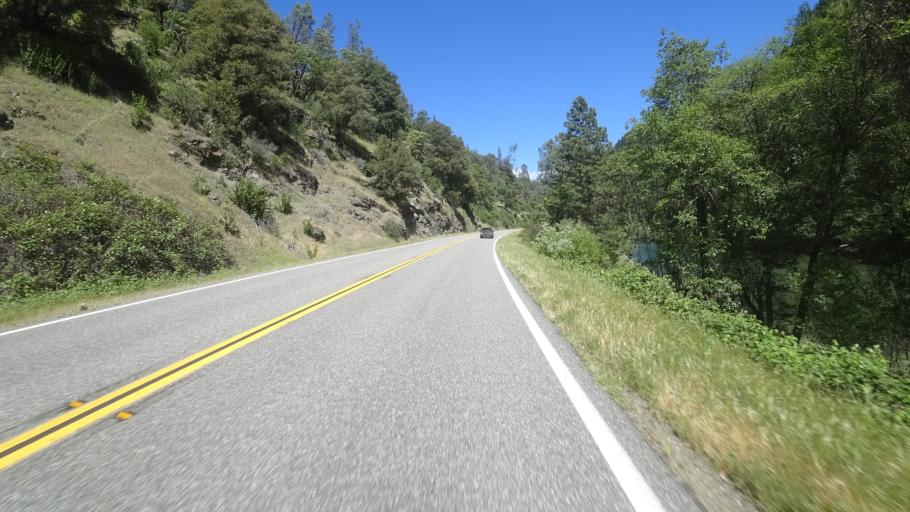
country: US
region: California
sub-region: Trinity County
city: Hayfork
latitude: 40.7553
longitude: -123.1563
